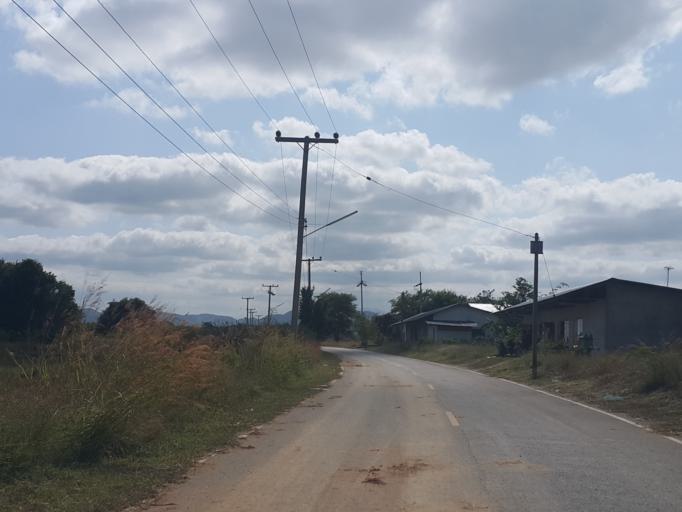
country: TH
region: Lamphun
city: Ban Thi
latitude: 18.5627
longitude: 99.0860
